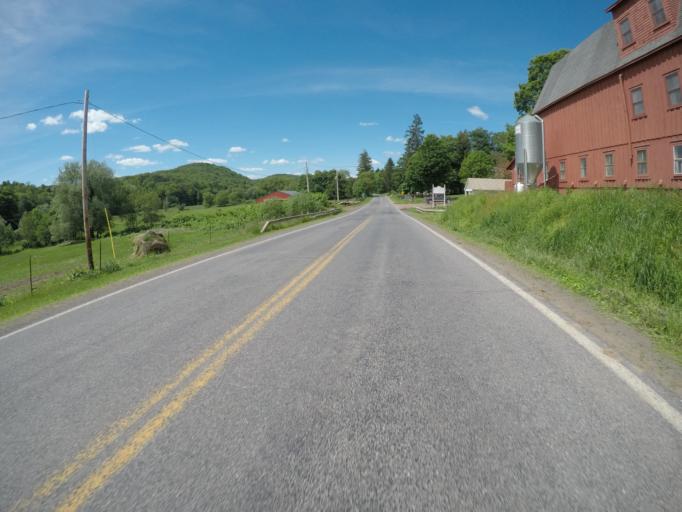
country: US
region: New York
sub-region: Delaware County
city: Delhi
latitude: 42.1665
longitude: -74.7888
